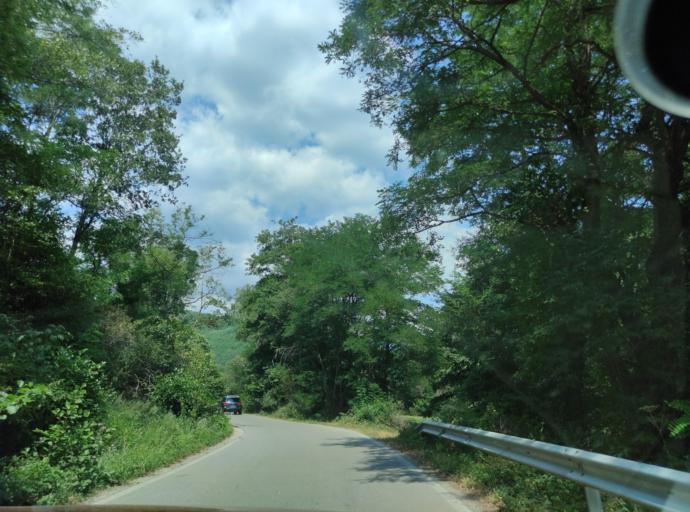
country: BG
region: Blagoevgrad
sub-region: Obshtina Belitsa
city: Belitsa
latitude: 41.9965
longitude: 23.5495
